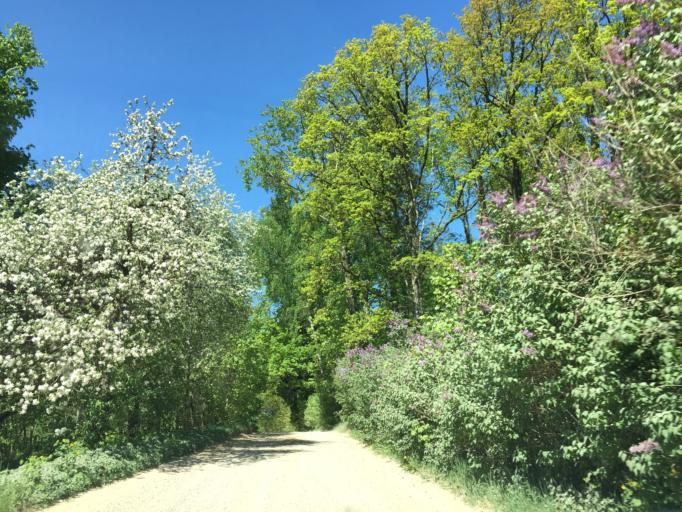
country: LV
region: Ikskile
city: Ikskile
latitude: 56.8562
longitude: 24.5070
